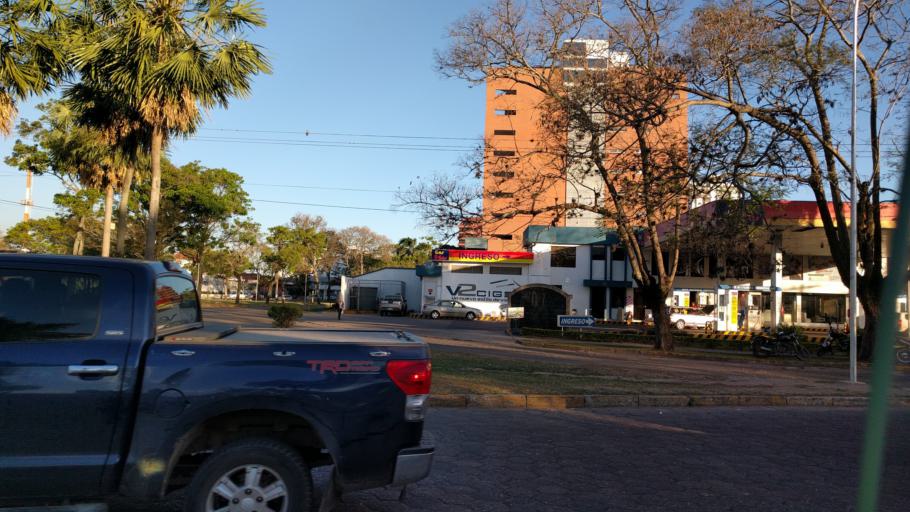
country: BO
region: Santa Cruz
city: Santa Cruz de la Sierra
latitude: -17.7624
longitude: -63.1921
